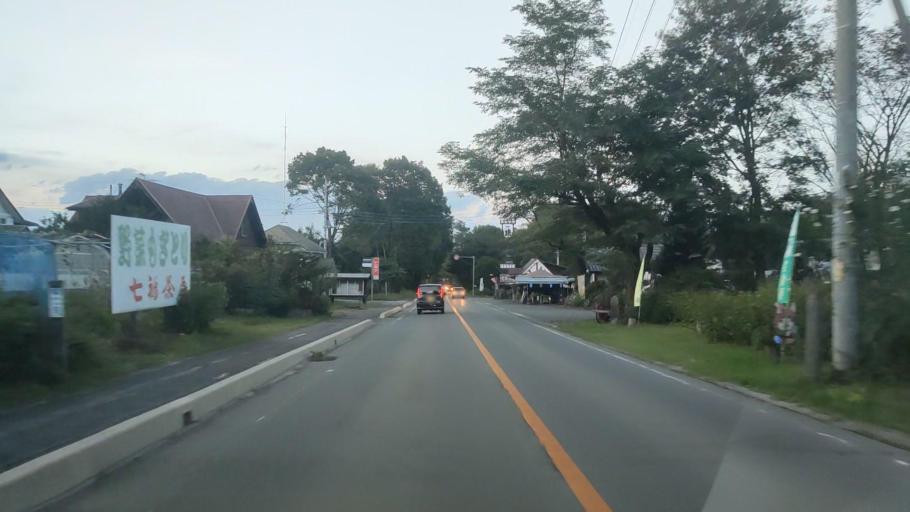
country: JP
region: Nagano
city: Komoro
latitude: 36.4982
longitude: 138.5857
